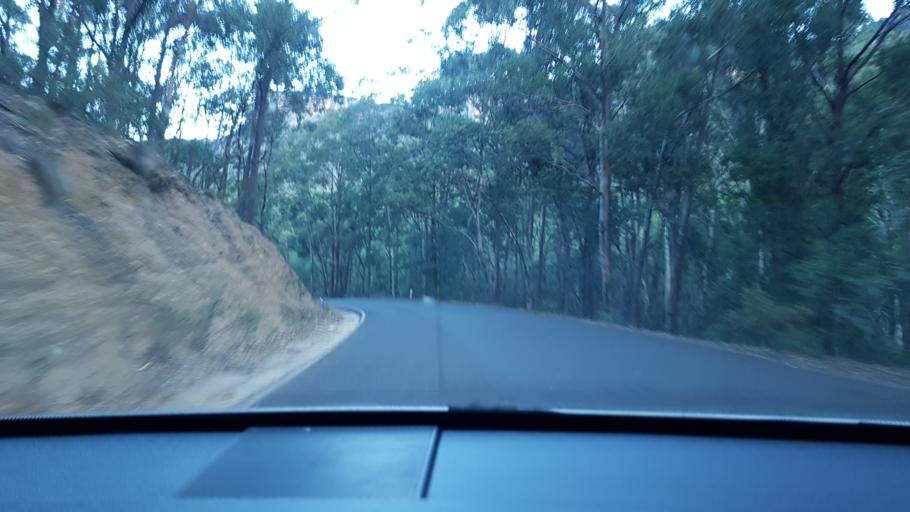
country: AU
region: New South Wales
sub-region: Lithgow
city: Portland
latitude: -33.3057
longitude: 150.1186
